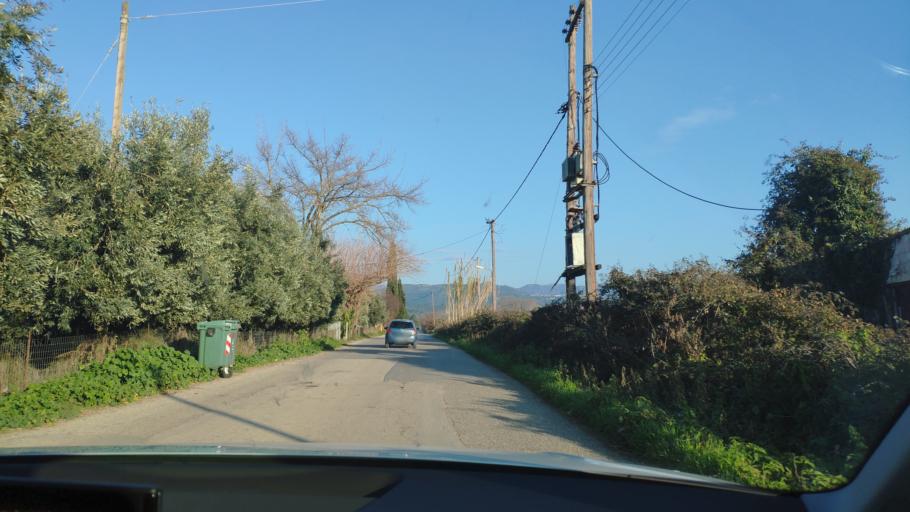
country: GR
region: West Greece
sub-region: Nomos Aitolias kai Akarnanias
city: Krikellos
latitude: 38.9300
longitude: 21.1593
